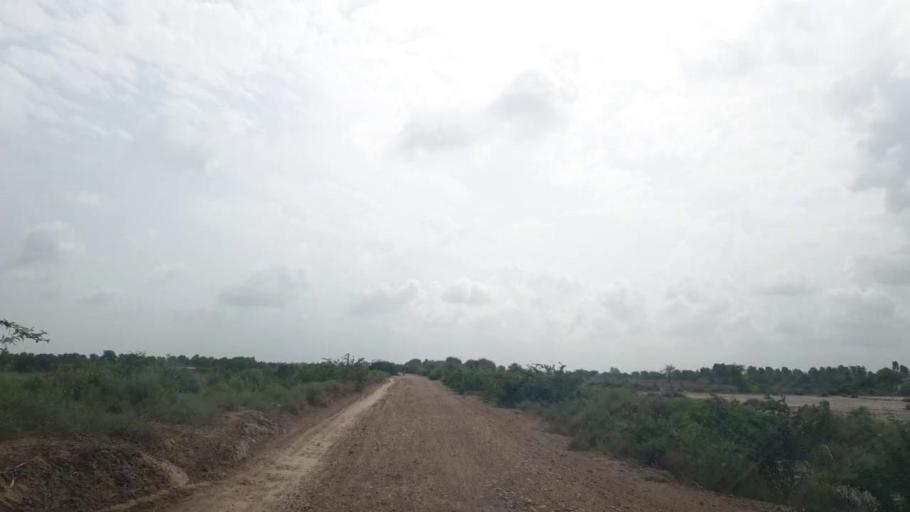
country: PK
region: Sindh
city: Tando Bago
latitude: 24.8157
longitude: 69.0434
